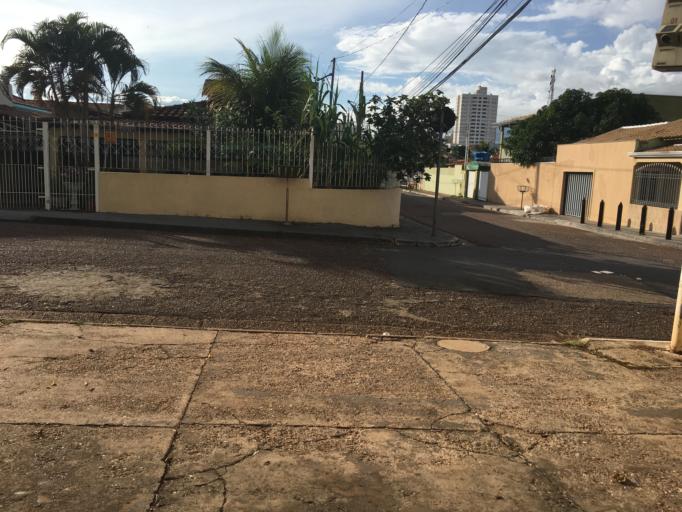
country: BR
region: Mato Grosso
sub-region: Cuiaba
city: Cuiaba
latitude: -15.5977
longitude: -56.0790
